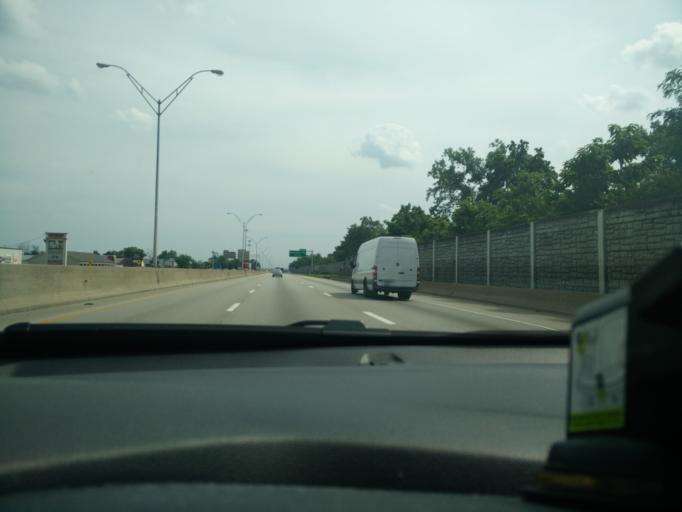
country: US
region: Ohio
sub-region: Montgomery County
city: Northridge
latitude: 39.8306
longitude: -84.1897
